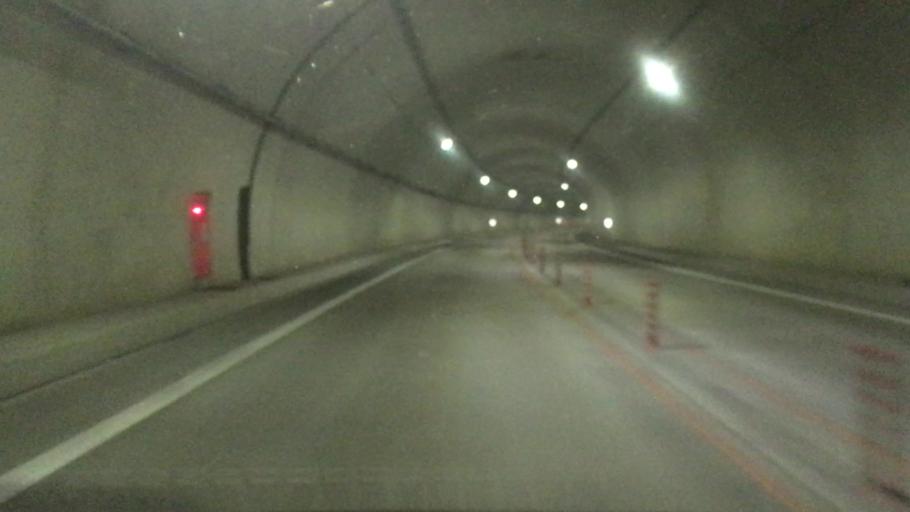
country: JP
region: Hyogo
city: Toyooka
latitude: 35.6266
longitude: 134.5207
